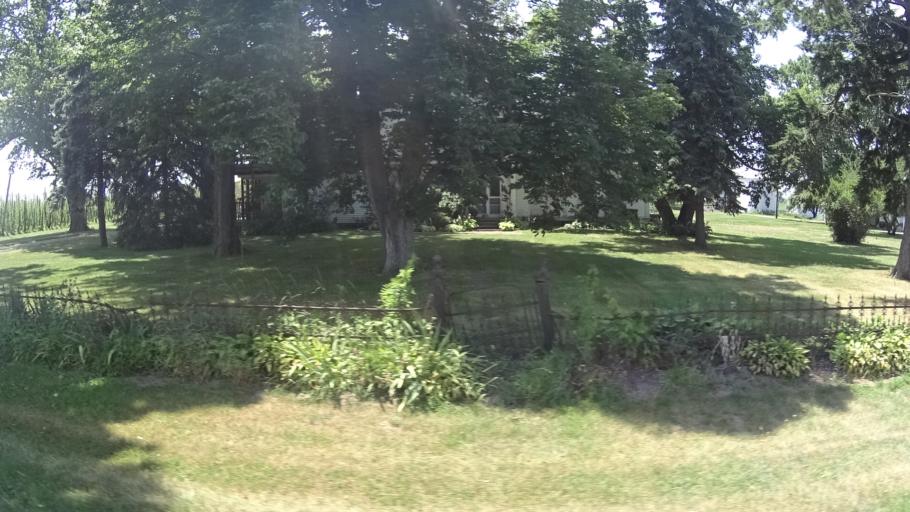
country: US
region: Ohio
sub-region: Erie County
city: Sandusky
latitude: 41.3857
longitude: -82.7874
